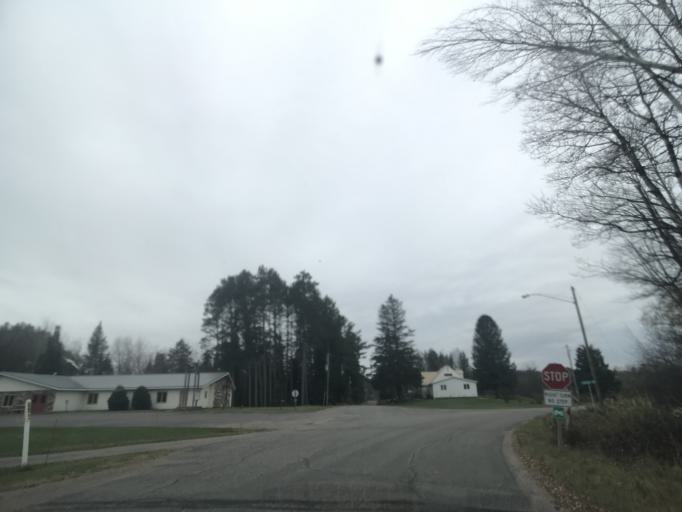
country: US
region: Wisconsin
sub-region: Menominee County
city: Legend Lake
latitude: 45.1810
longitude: -88.4679
